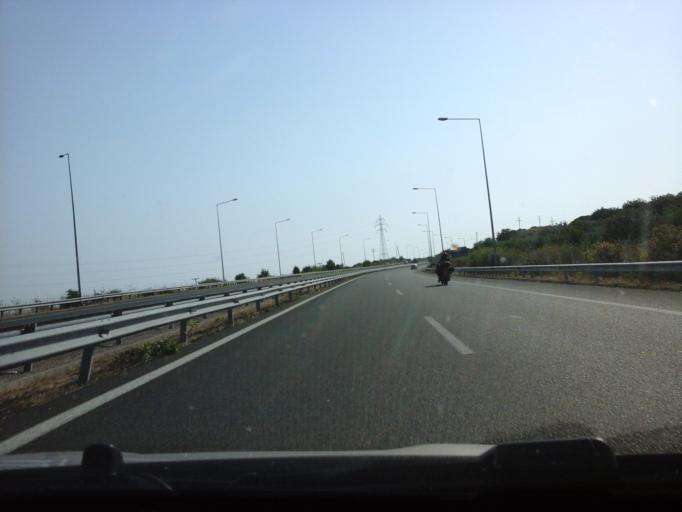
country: GR
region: East Macedonia and Thrace
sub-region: Nomos Evrou
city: Alexandroupoli
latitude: 40.8618
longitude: 25.7589
